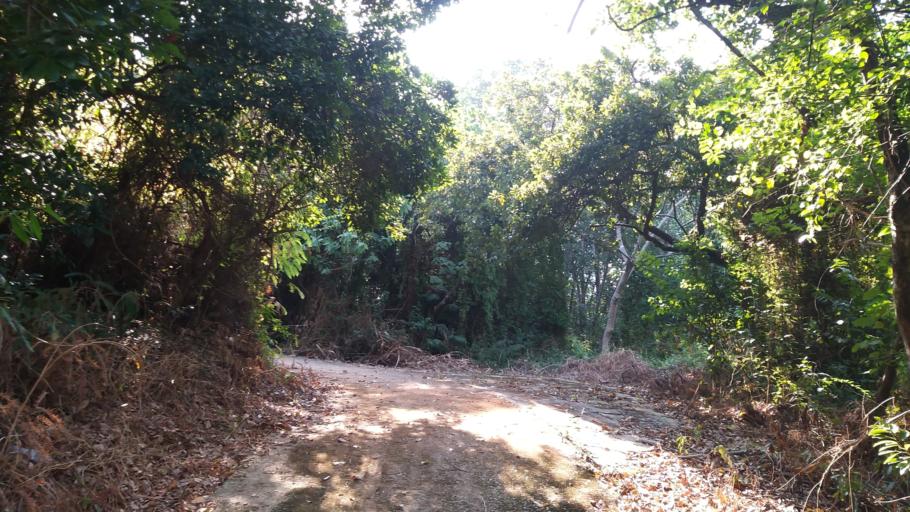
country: HK
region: Tuen Mun
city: Tuen Mun
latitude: 22.4045
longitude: 113.9648
